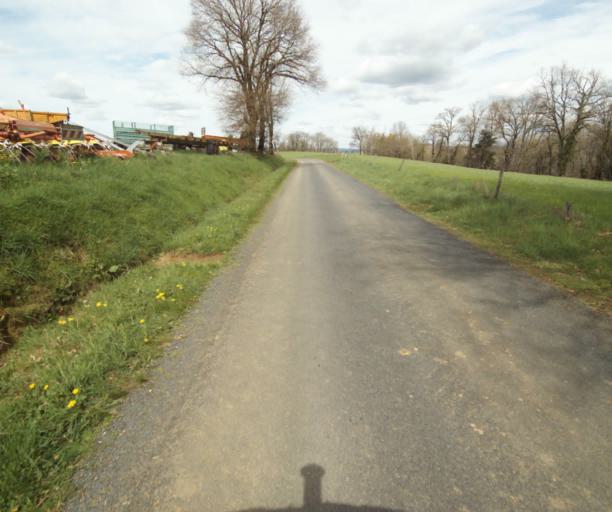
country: FR
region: Limousin
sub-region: Departement de la Correze
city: Laguenne
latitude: 45.2143
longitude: 1.8545
